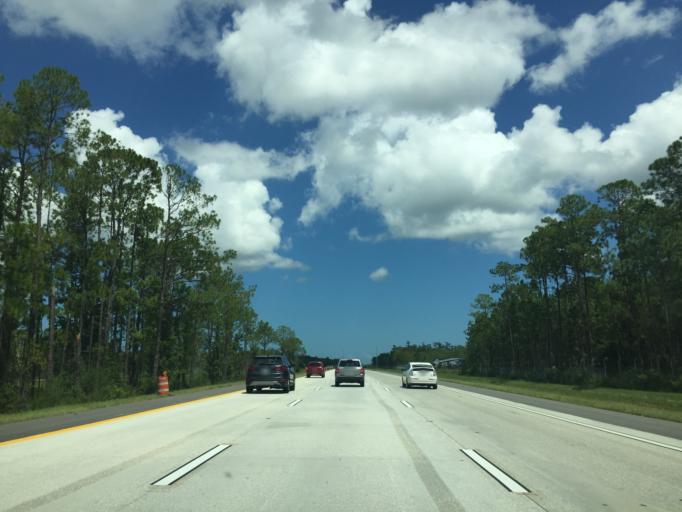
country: US
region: Florida
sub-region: Volusia County
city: Samsula-Spruce Creek
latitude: 29.0931
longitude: -81.1598
